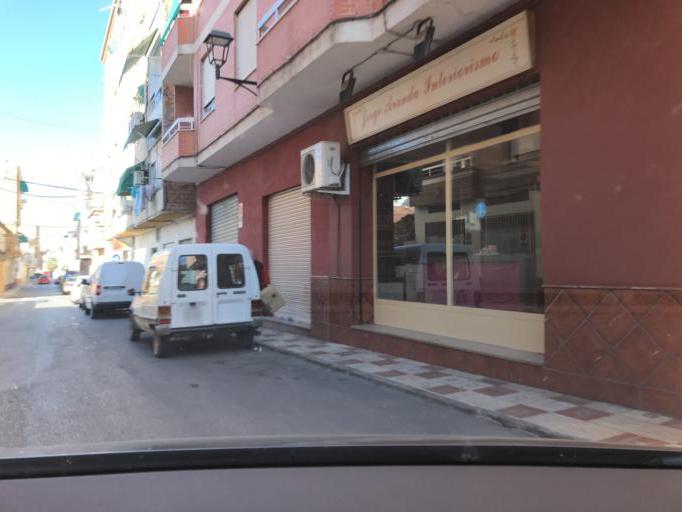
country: ES
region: Andalusia
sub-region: Provincia de Granada
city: Maracena
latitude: 37.2069
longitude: -3.6293
